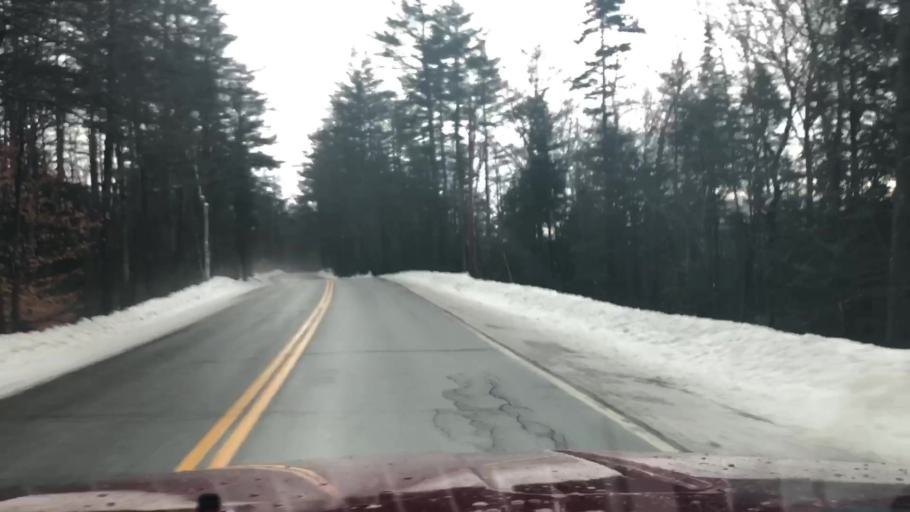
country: US
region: Maine
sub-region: Oxford County
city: West Paris
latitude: 44.4143
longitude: -70.6437
